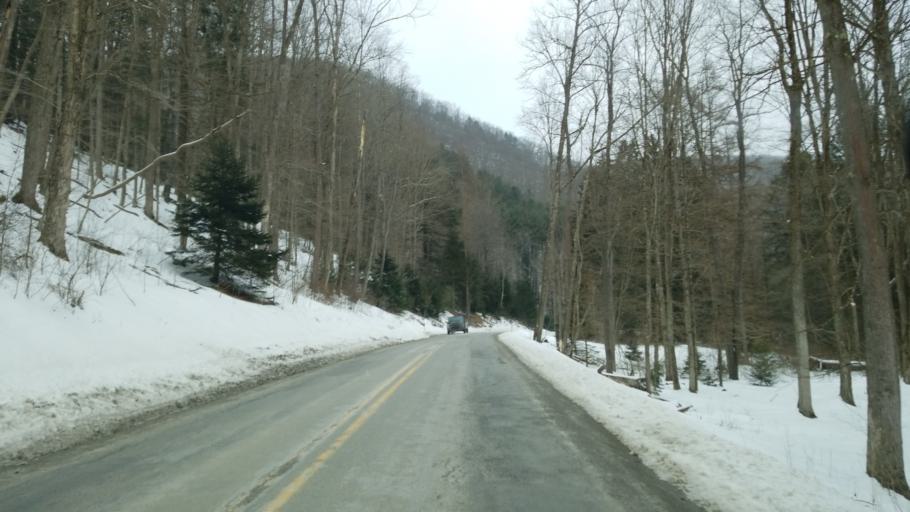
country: US
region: Pennsylvania
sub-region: Cameron County
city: Emporium
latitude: 41.2770
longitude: -78.1407
